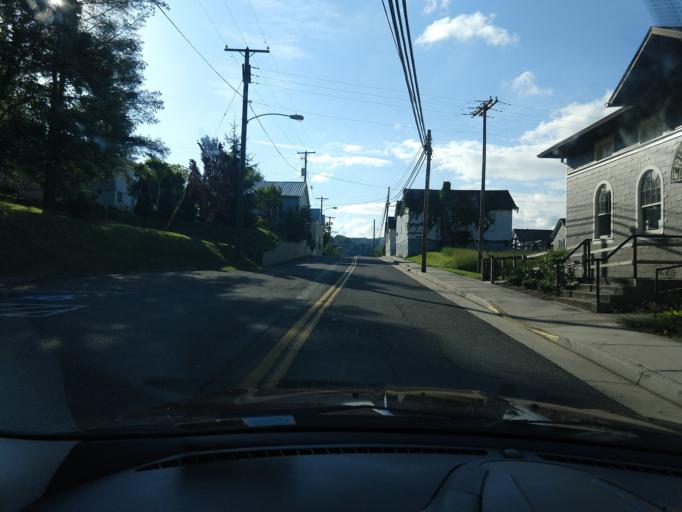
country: US
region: Virginia
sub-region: City of Galax
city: Galax
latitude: 36.7166
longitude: -80.9782
